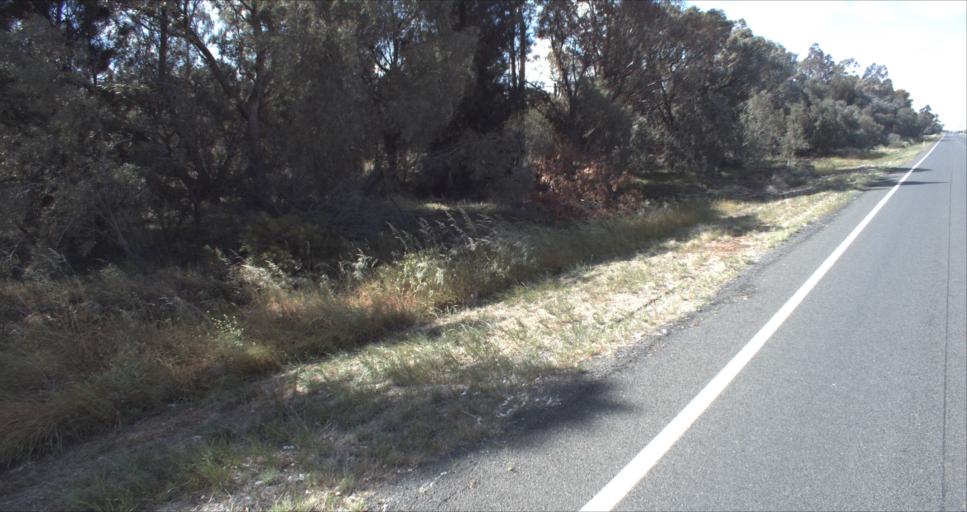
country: AU
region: New South Wales
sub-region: Murrumbidgee Shire
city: Darlington Point
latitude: -34.5285
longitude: 146.1744
